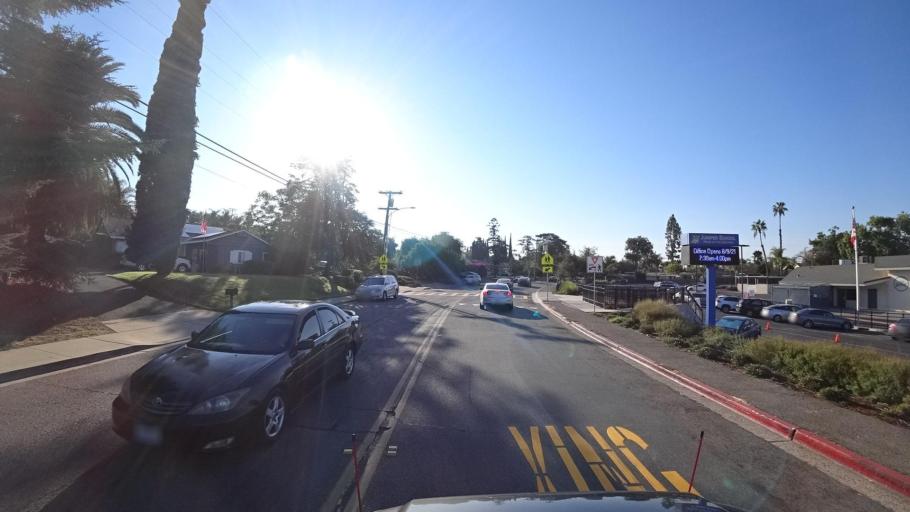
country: US
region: California
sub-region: San Diego County
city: Escondido
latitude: 33.1057
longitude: -117.0678
